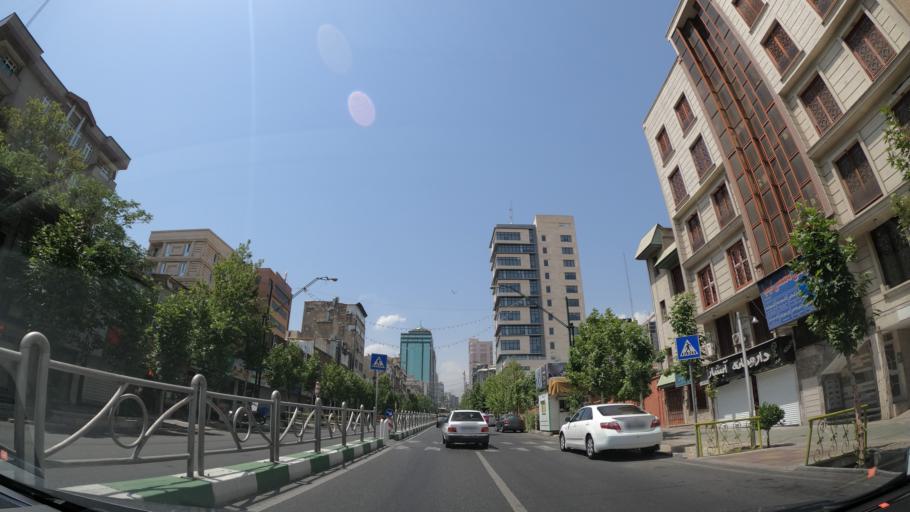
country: IR
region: Tehran
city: Tehran
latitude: 35.7294
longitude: 51.4126
